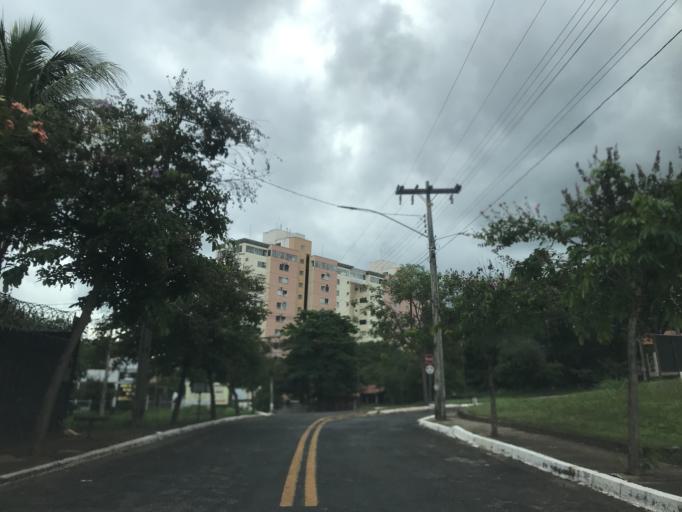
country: BR
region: Goias
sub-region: Caldas Novas
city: Caldas Novas
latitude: -17.7690
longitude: -48.7580
